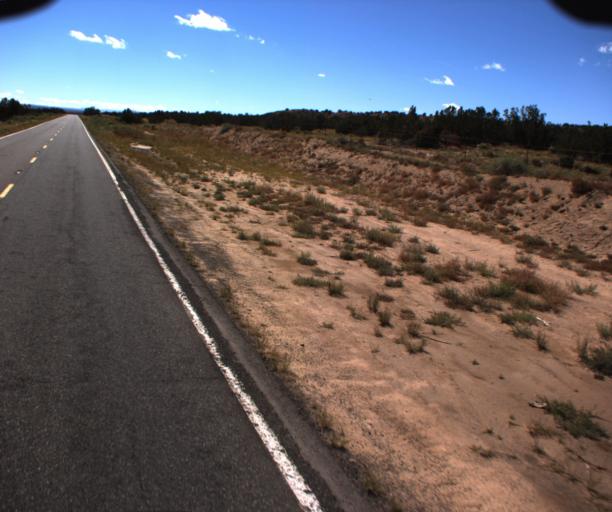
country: US
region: Arizona
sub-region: Apache County
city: Saint Johns
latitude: 34.7913
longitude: -109.2382
